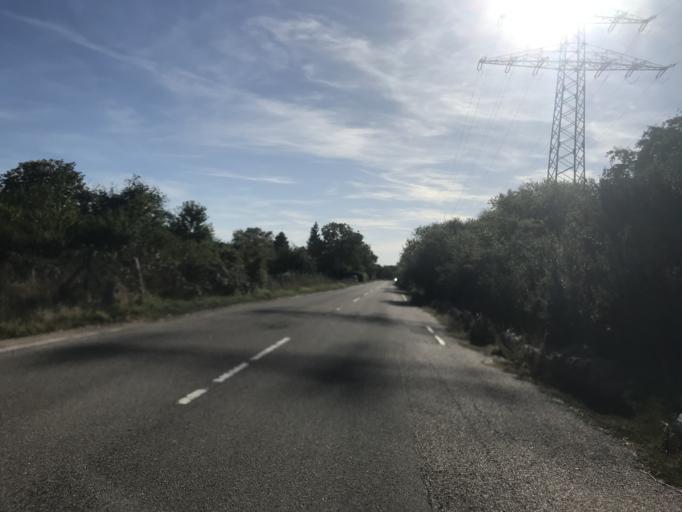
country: DE
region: Hesse
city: Kelsterbach
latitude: 50.0813
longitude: 8.5539
